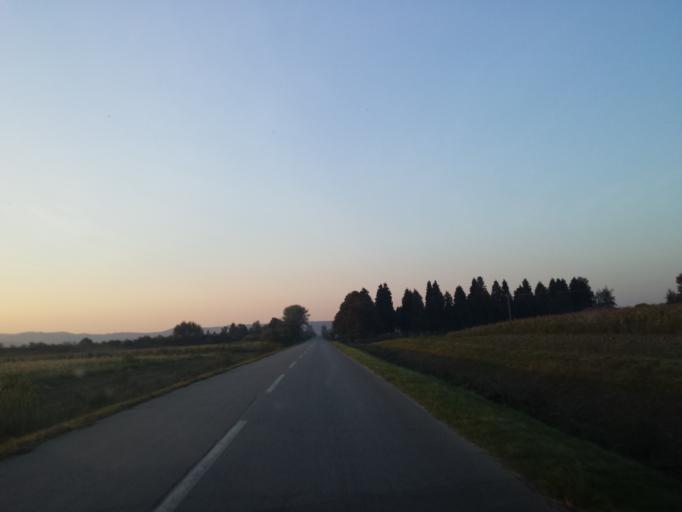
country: HR
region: Brodsko-Posavska
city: Oriovac
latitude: 45.1302
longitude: 17.8225
